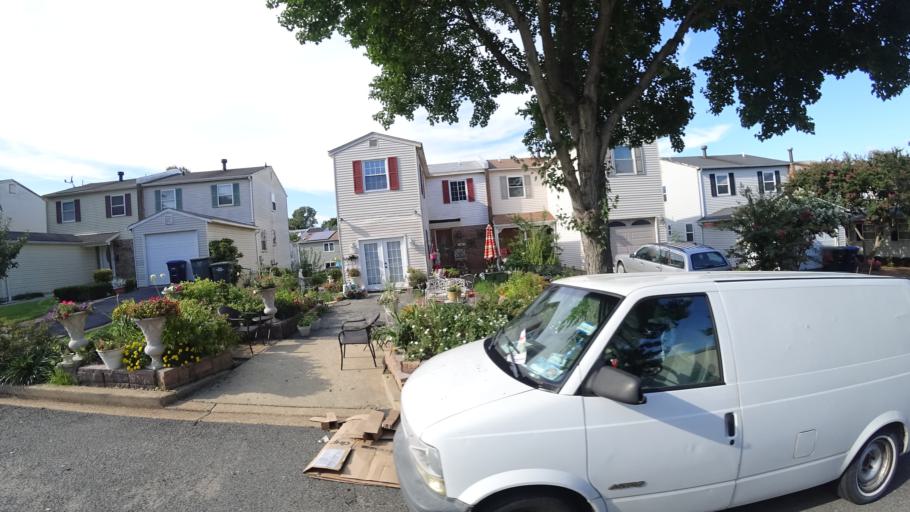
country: US
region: Maryland
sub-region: Prince George's County
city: Chillum
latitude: 38.9456
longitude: -76.9977
